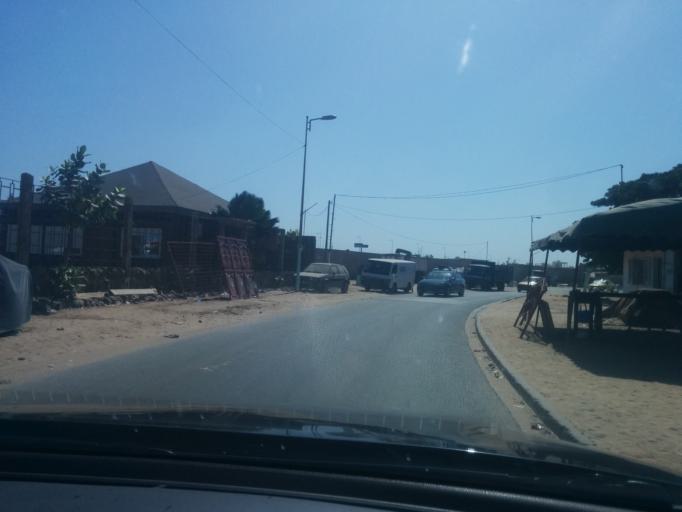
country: SN
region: Dakar
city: Grand Dakar
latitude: 14.7418
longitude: -17.4410
